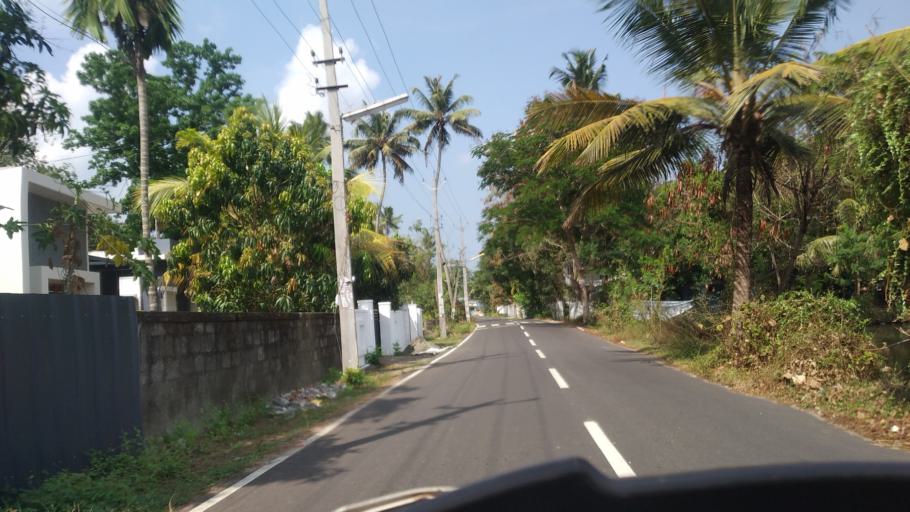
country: IN
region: Kerala
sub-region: Ernakulam
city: Elur
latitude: 10.1127
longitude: 76.2300
